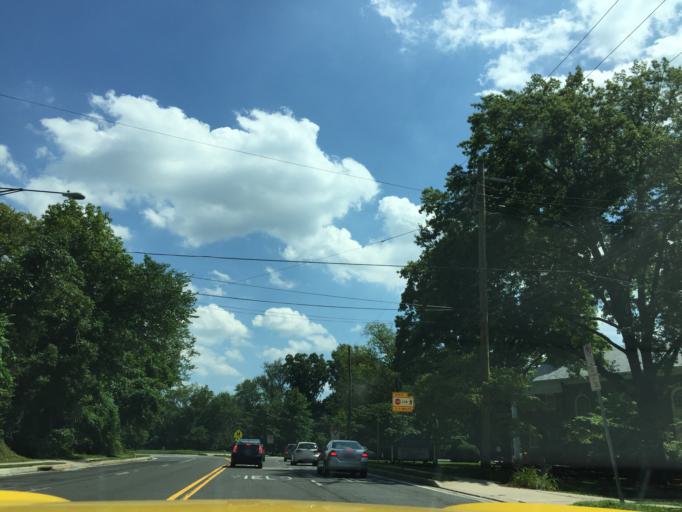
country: US
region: Maryland
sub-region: Montgomery County
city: Somerset
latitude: 38.9501
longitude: -77.1015
